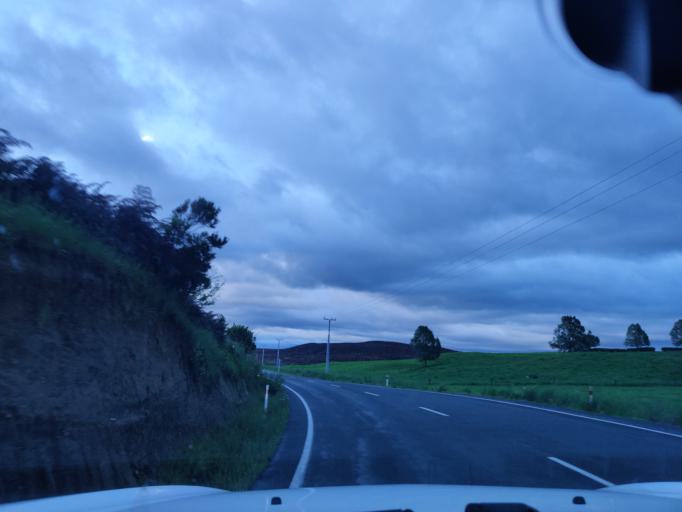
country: NZ
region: Waikato
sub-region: South Waikato District
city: Tokoroa
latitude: -38.1641
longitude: 175.7668
